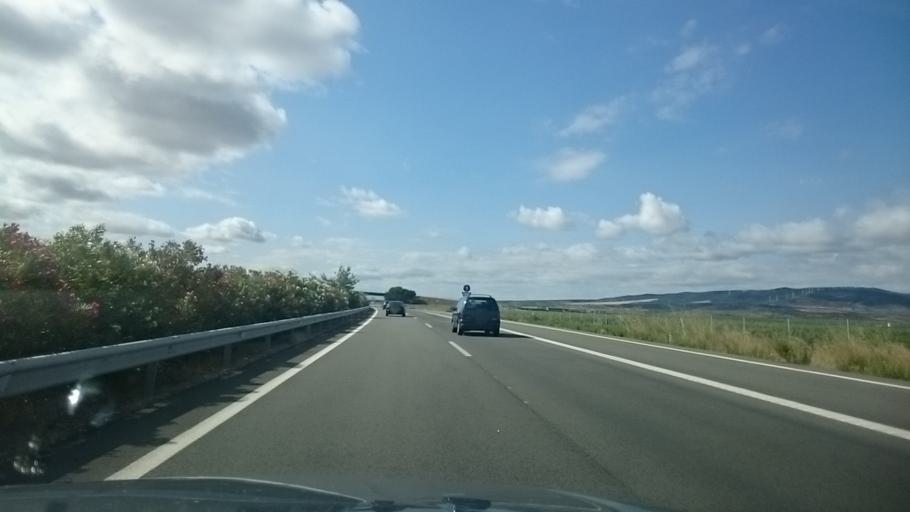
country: ES
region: La Rioja
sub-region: Provincia de La Rioja
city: Aldeanueva de Ebro
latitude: 42.2341
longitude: -1.9013
